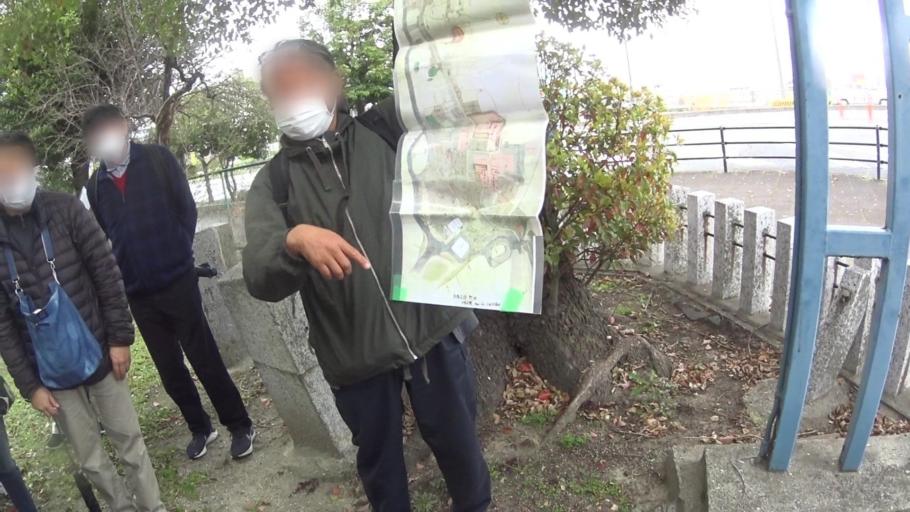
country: JP
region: Aichi
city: Nagoya-shi
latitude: 35.1163
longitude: 136.9114
